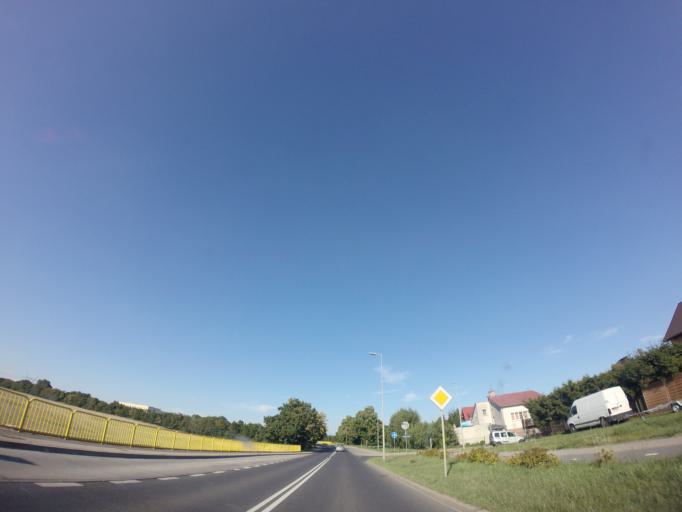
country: PL
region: Lubusz
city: Gorzow Wielkopolski
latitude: 52.7444
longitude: 15.2819
